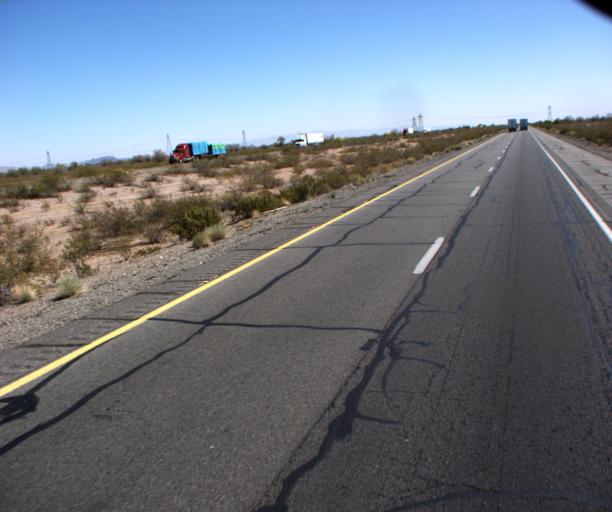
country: US
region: Arizona
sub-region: Maricopa County
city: Buckeye
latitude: 33.5163
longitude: -113.0461
